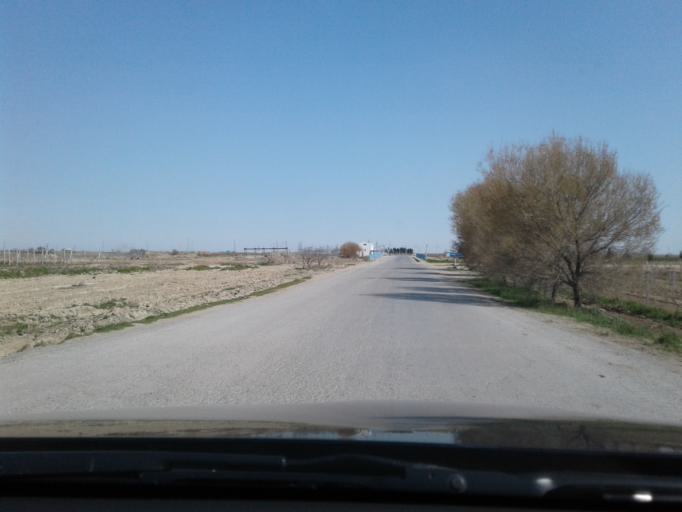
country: TM
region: Ahal
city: Abadan
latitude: 38.0946
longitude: 58.1991
